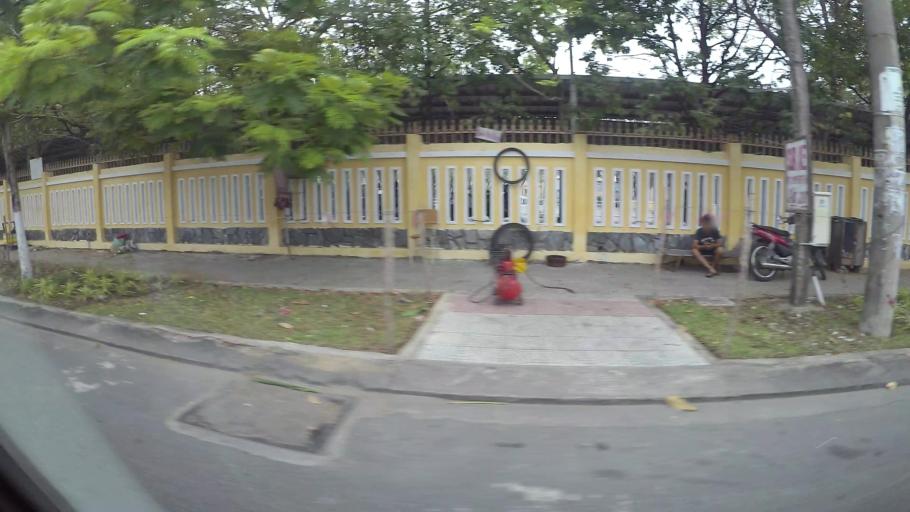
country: VN
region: Da Nang
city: Son Tra
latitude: 16.0469
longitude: 108.2390
